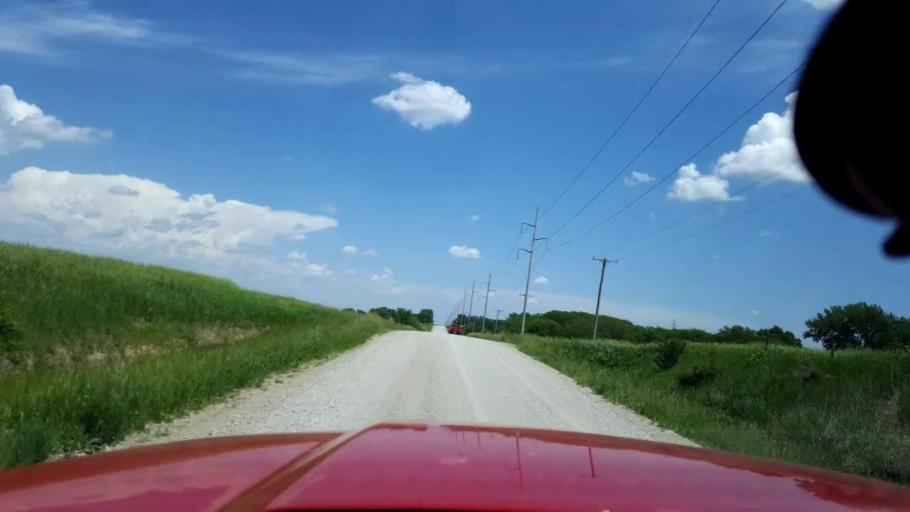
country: US
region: Iowa
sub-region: Story County
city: Gilbert
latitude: 42.0492
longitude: -93.7546
